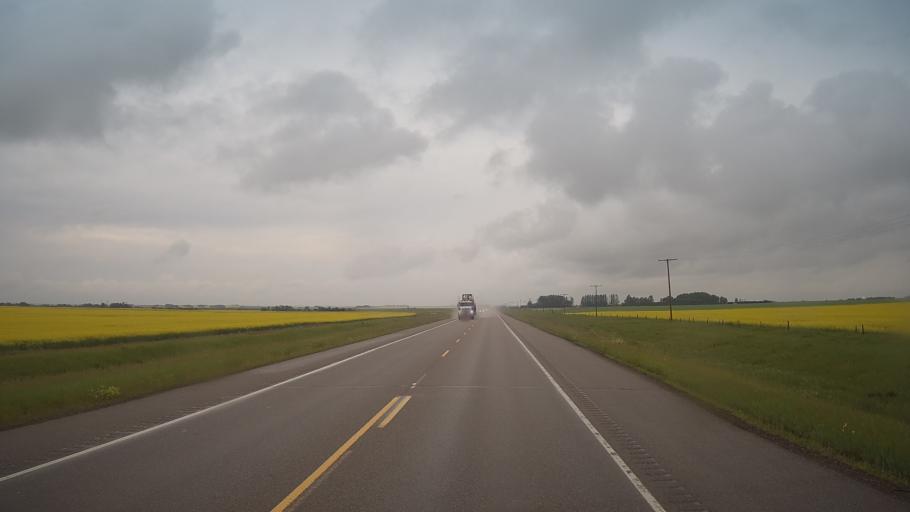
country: CA
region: Saskatchewan
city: Unity
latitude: 52.4348
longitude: -108.9603
